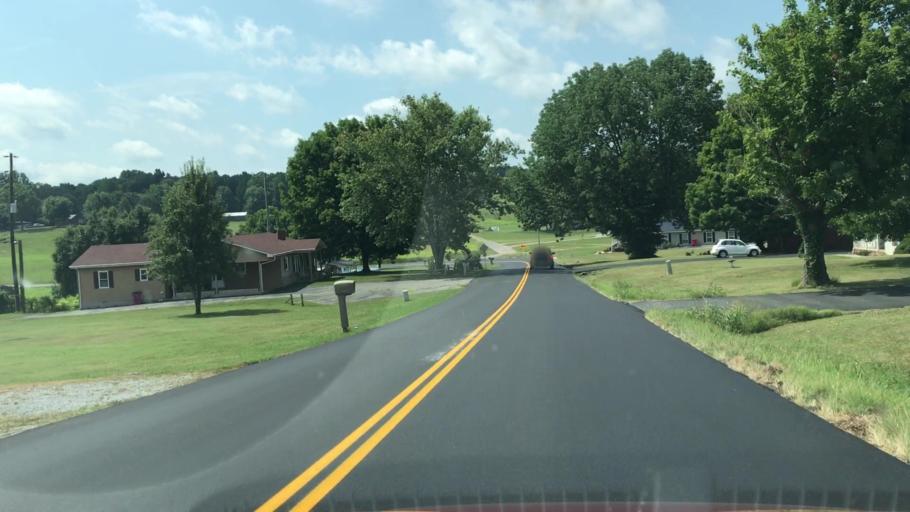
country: US
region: Kentucky
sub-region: Monroe County
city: Tompkinsville
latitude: 36.7201
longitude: -85.7193
